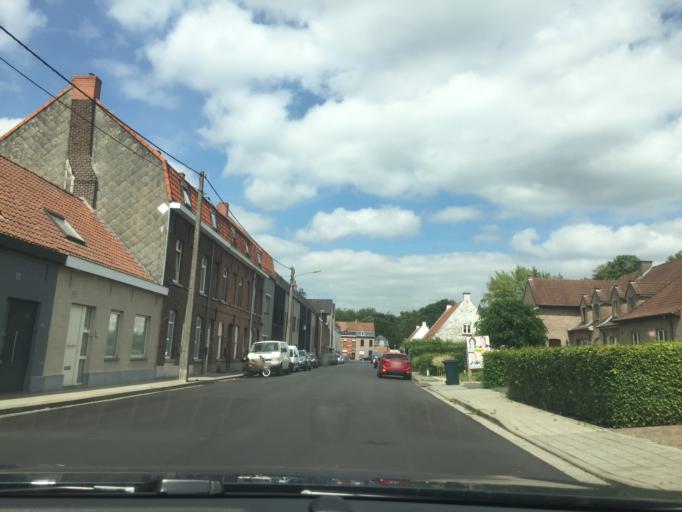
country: BE
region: Flanders
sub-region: Provincie West-Vlaanderen
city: Zwevegem
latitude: 50.8114
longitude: 3.3291
